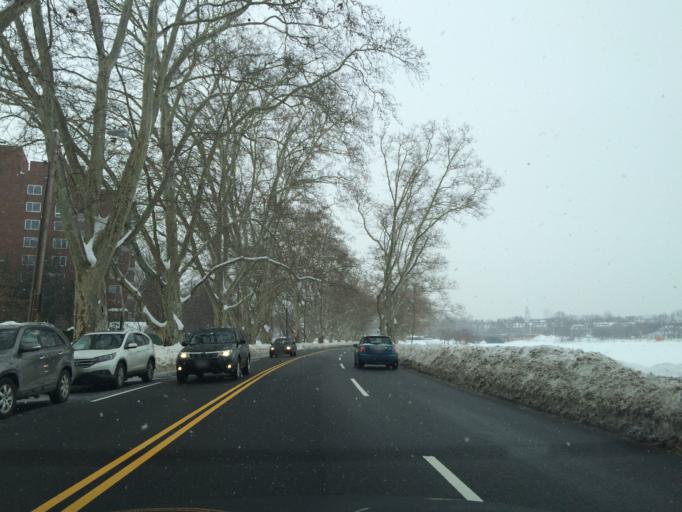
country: US
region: Massachusetts
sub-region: Middlesex County
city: Cambridge
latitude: 42.3724
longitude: -71.1254
